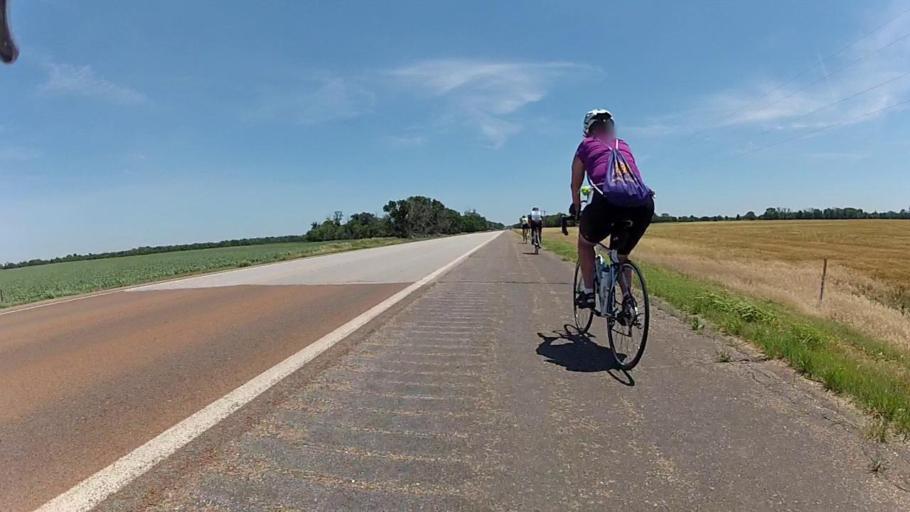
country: US
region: Kansas
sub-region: Barber County
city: Medicine Lodge
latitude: 37.2534
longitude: -98.3398
